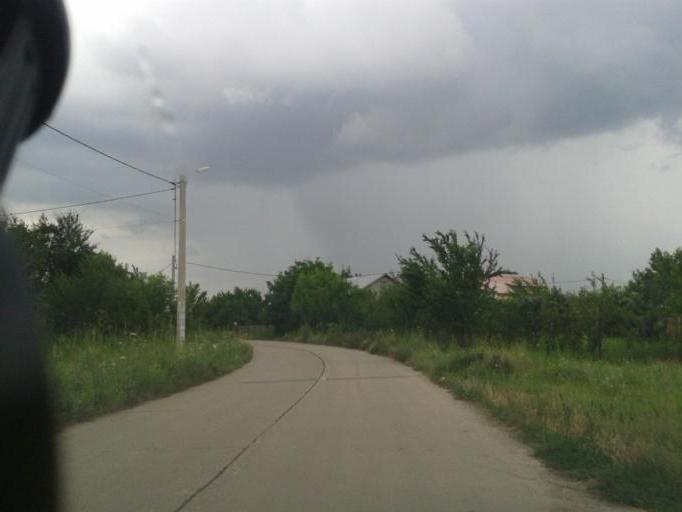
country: RO
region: Ialomita
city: Sinesti
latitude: 44.5464
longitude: 26.4333
